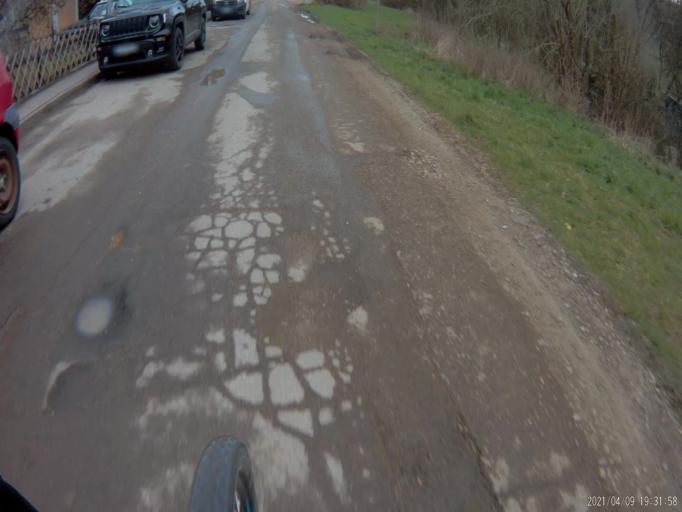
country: DE
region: Baden-Wuerttemberg
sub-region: Regierungsbezirk Stuttgart
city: Neuhausen auf den Fildern
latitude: 48.6803
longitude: 9.2933
